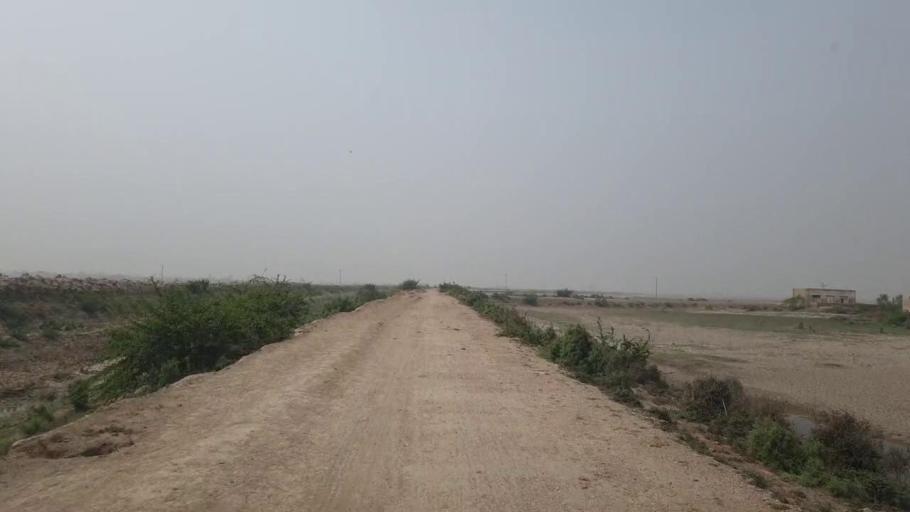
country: PK
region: Sindh
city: Kario
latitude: 24.6653
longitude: 68.6487
